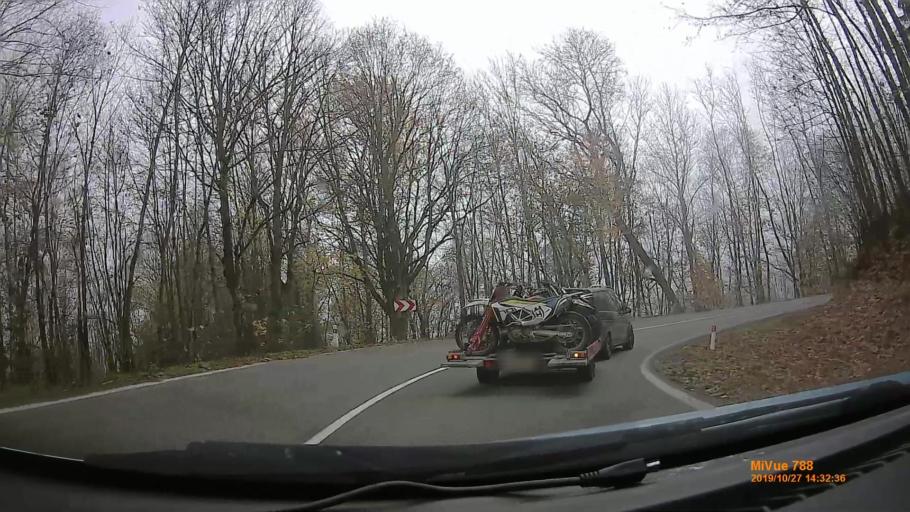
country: CZ
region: Olomoucky
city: Olsany
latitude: 49.9853
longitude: 16.8152
